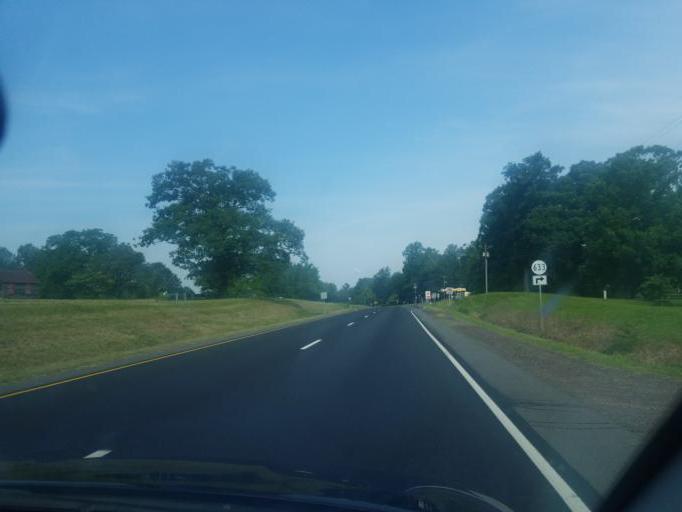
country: US
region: Virginia
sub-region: Culpeper County
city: Merrimac
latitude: 38.4561
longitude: -78.1143
